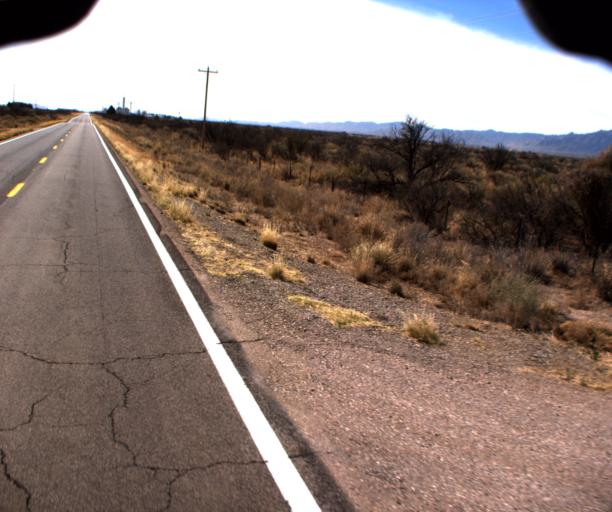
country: US
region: Arizona
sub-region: Cochise County
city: Willcox
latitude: 32.0980
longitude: -109.9102
